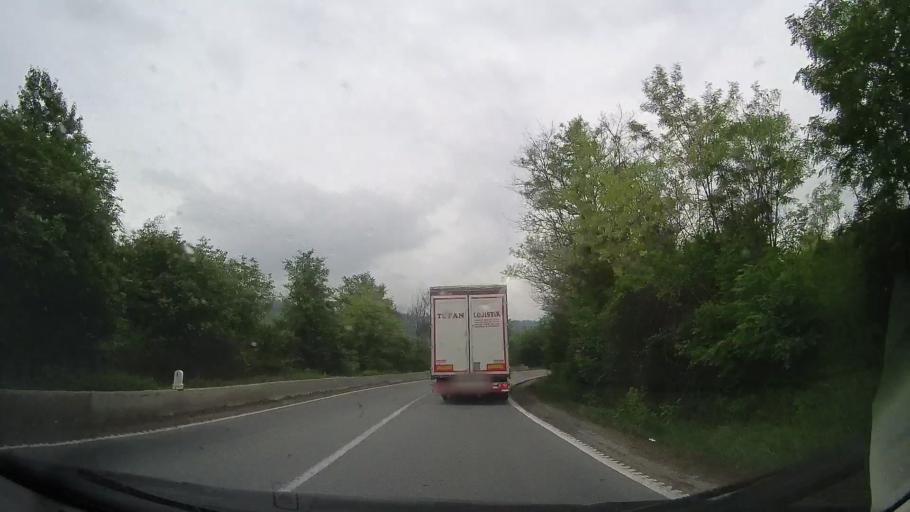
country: RO
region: Caras-Severin
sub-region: Comuna Mehadia
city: Plugova
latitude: 44.9684
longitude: 22.3527
